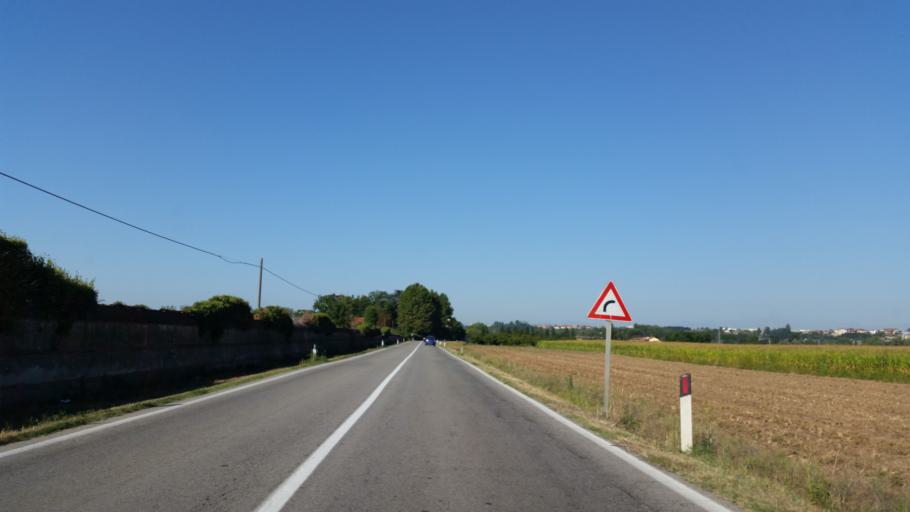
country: IT
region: Piedmont
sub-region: Provincia di Cuneo
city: Bra
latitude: 44.6788
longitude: 7.8791
